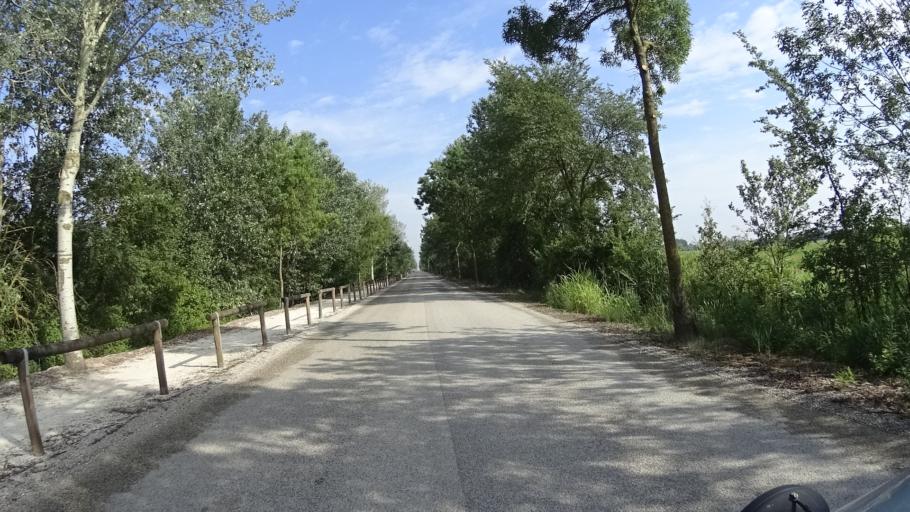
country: IT
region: Veneto
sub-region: Provincia di Venezia
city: Bibione
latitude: 45.6269
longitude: 12.9571
